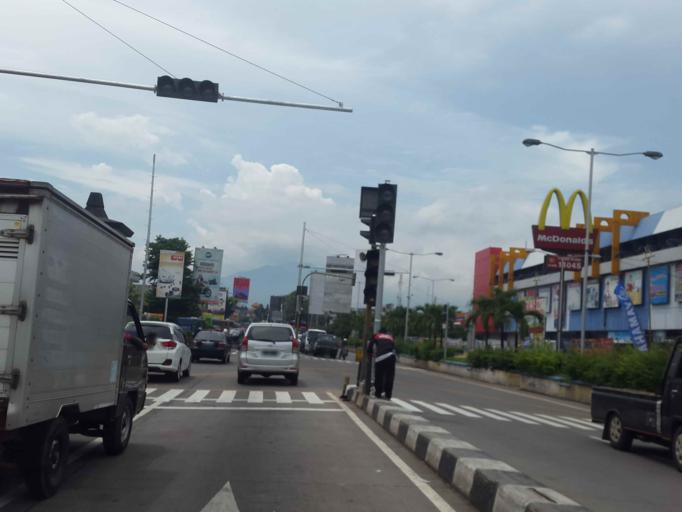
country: ID
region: Central Java
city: Semarang
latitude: -7.0610
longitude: 110.4137
